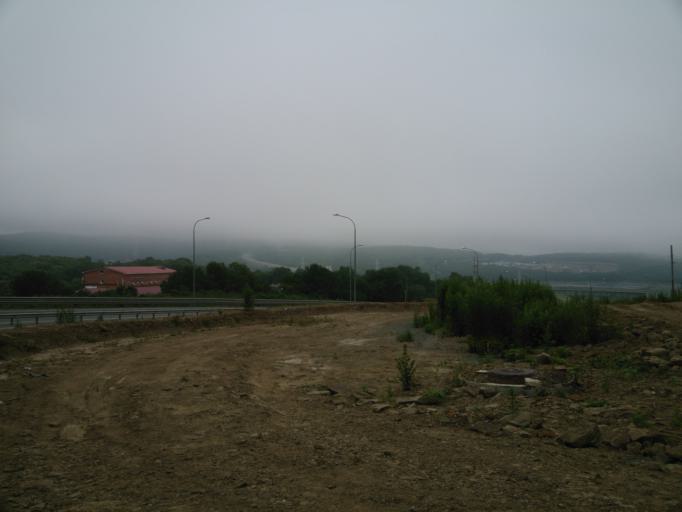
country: RU
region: Primorskiy
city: Vladivostok
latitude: 43.0980
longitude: 131.9831
